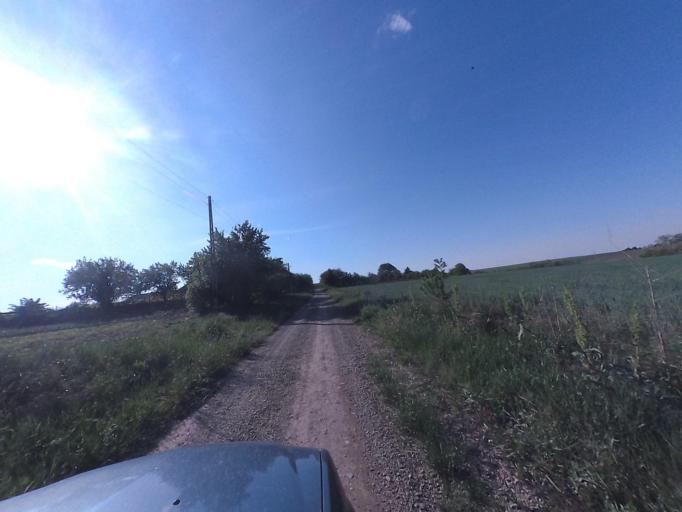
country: RO
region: Neamt
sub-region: Comuna Dulcesti
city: Dulcesti
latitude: 47.0016
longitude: 26.7763
